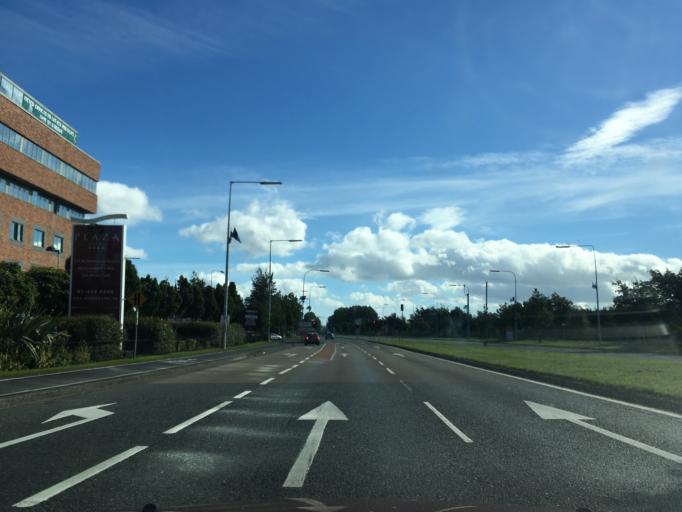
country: IE
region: Leinster
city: Tallaght
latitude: 53.2854
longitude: -6.3677
